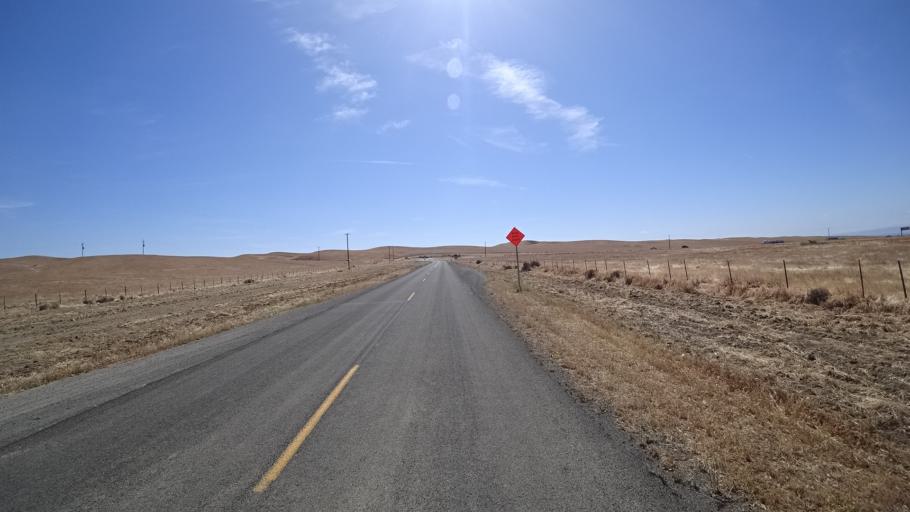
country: US
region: California
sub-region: Kings County
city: Kettleman City
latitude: 35.9352
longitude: -120.0214
